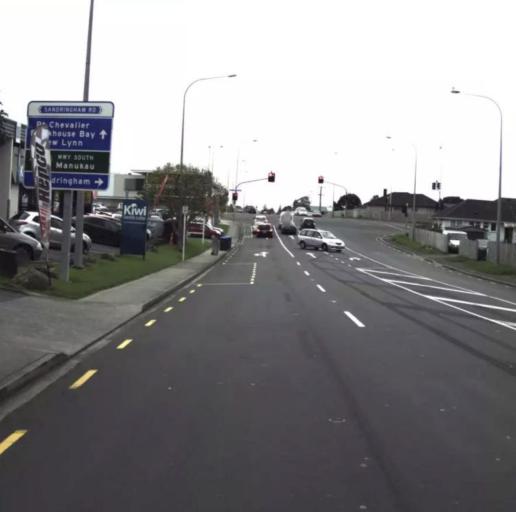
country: NZ
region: Auckland
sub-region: Auckland
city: Auckland
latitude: -36.9049
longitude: 174.7293
